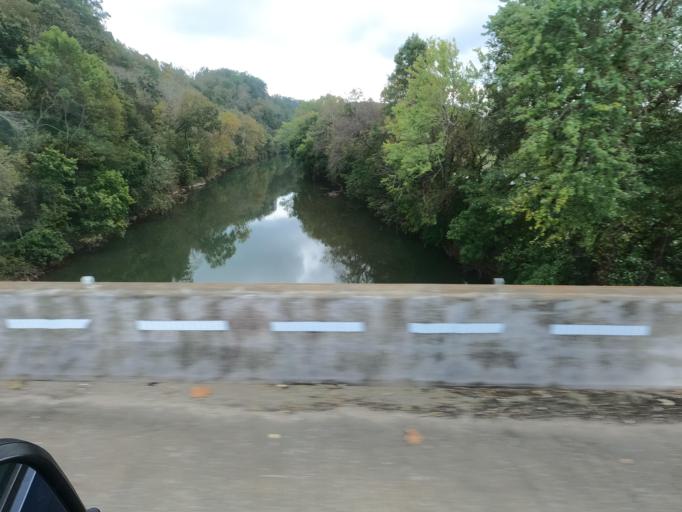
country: US
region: Tennessee
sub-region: Cheatham County
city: Pegram
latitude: 36.1071
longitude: -87.0740
